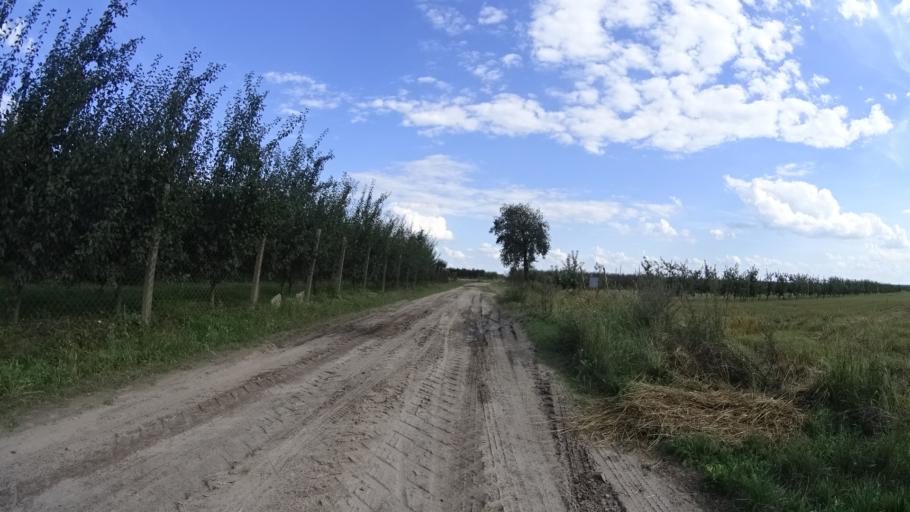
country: PL
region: Masovian Voivodeship
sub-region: Powiat bialobrzeski
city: Wysmierzyce
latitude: 51.6728
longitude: 20.7973
